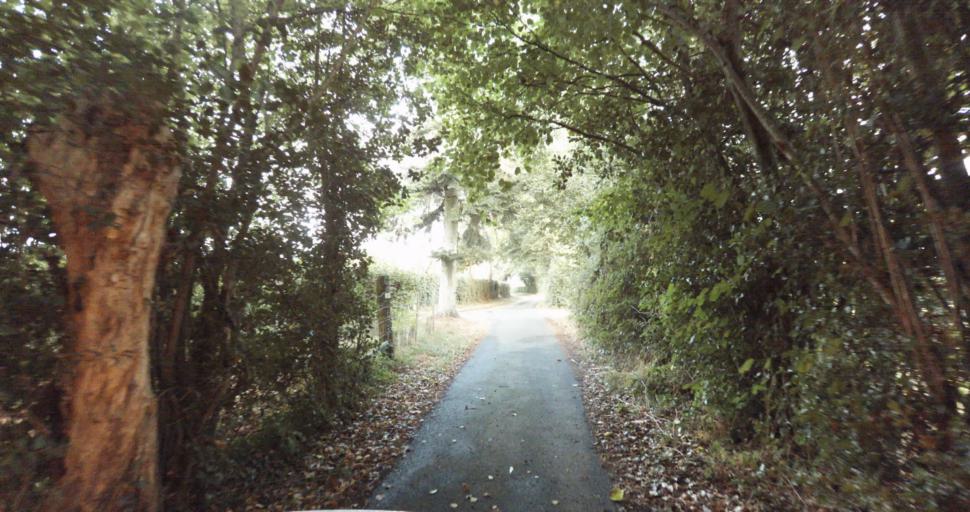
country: FR
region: Lower Normandy
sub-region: Departement de l'Orne
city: Vimoutiers
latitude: 48.9401
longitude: 0.2155
